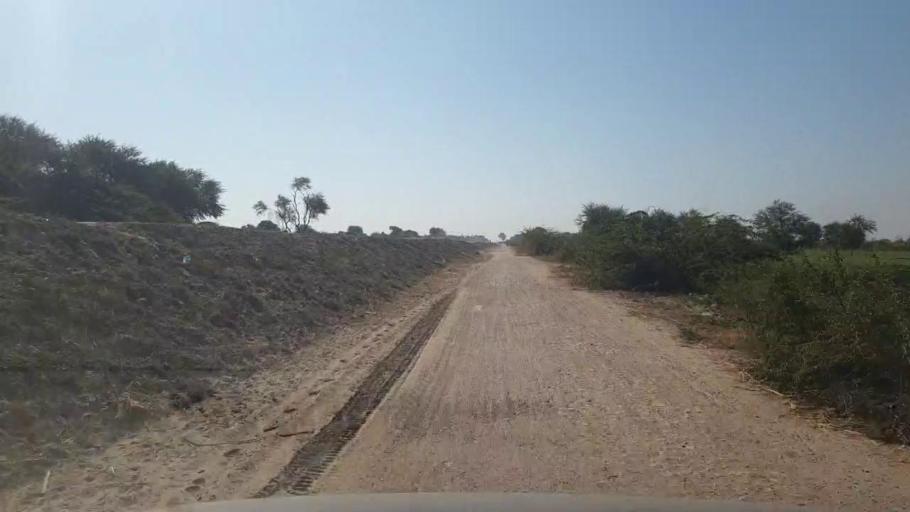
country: PK
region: Sindh
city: Mirwah Gorchani
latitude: 25.2894
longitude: 69.1032
